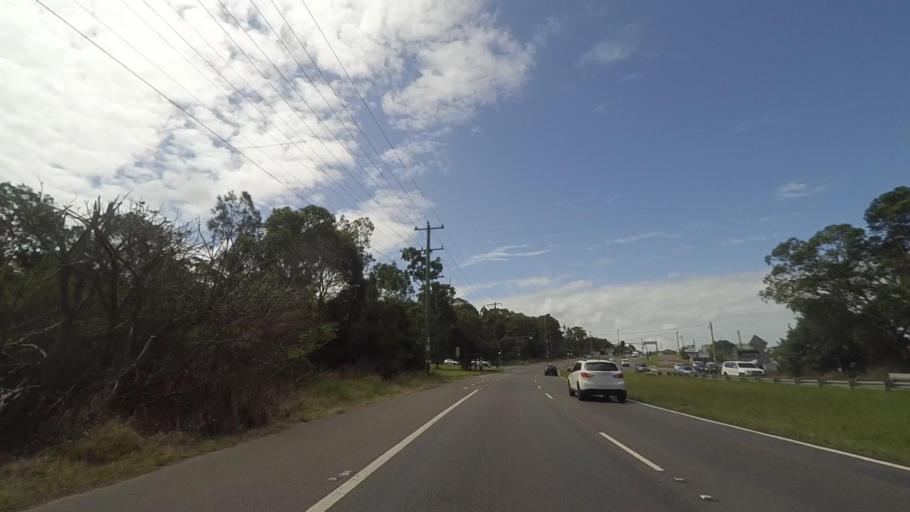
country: AU
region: New South Wales
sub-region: Lake Macquarie Shire
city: Windale
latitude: -33.0003
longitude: 151.6857
